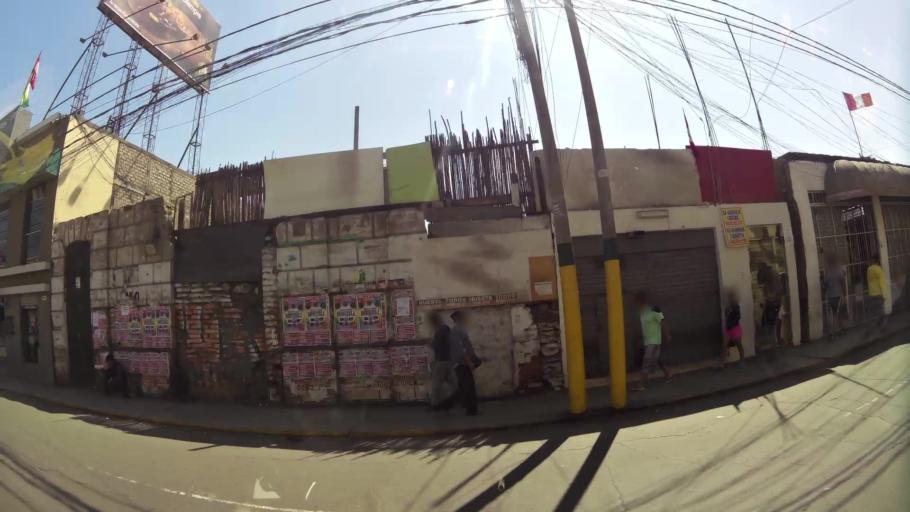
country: PE
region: Ica
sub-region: Provincia de Ica
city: Ica
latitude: -14.0643
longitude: -75.7316
